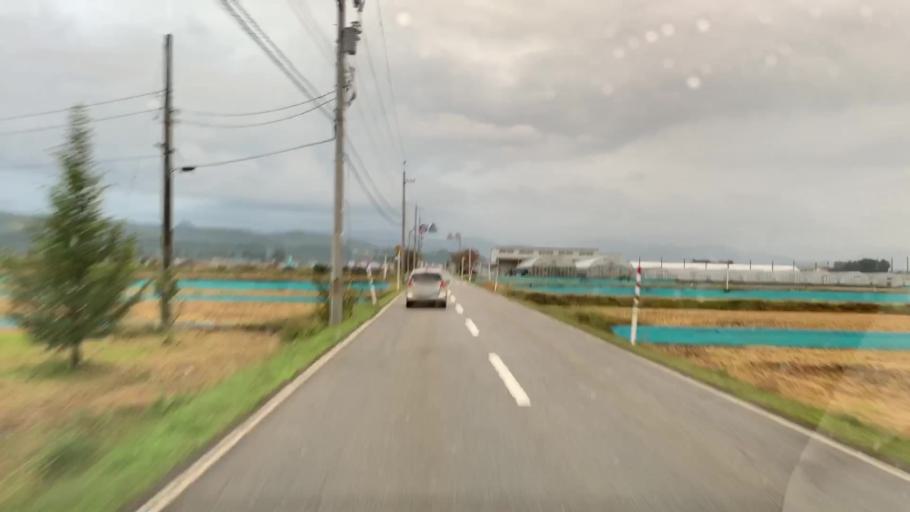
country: JP
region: Toyama
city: Kamiichi
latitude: 36.6398
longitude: 137.3285
